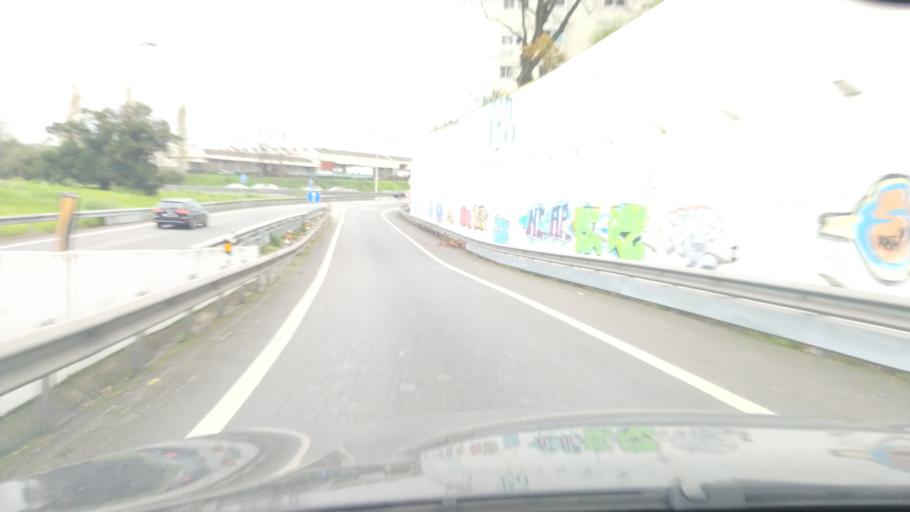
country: PT
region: Porto
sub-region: Matosinhos
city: Senhora da Hora
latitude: 41.1671
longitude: -8.6404
